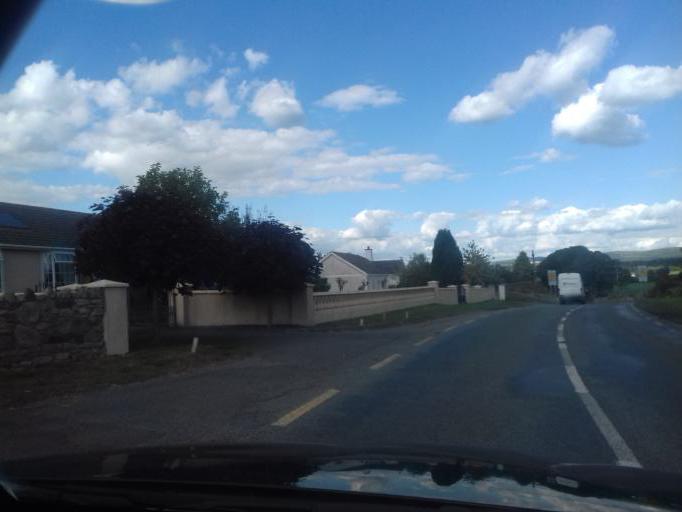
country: IE
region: Leinster
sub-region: Kilkenny
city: Thomastown
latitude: 52.5176
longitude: -7.1457
